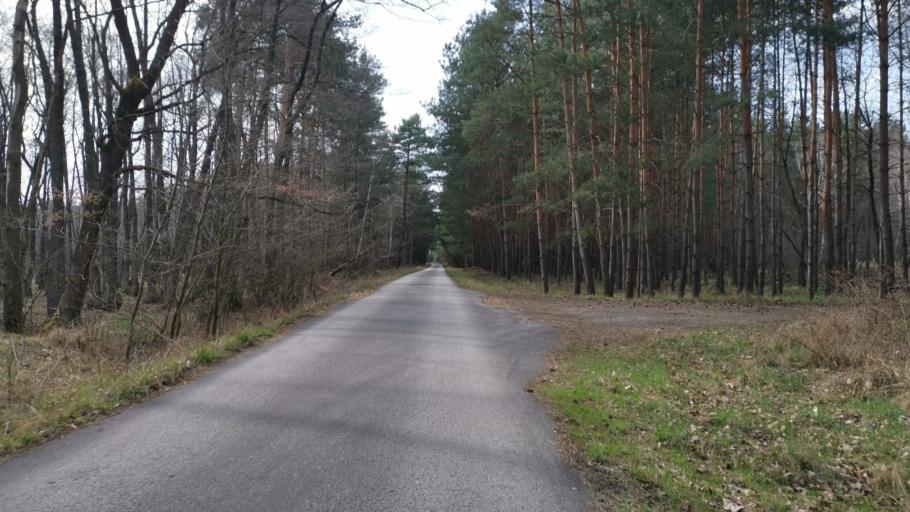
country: SK
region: Trnavsky
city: Gbely
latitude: 48.6886
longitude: 17.0568
